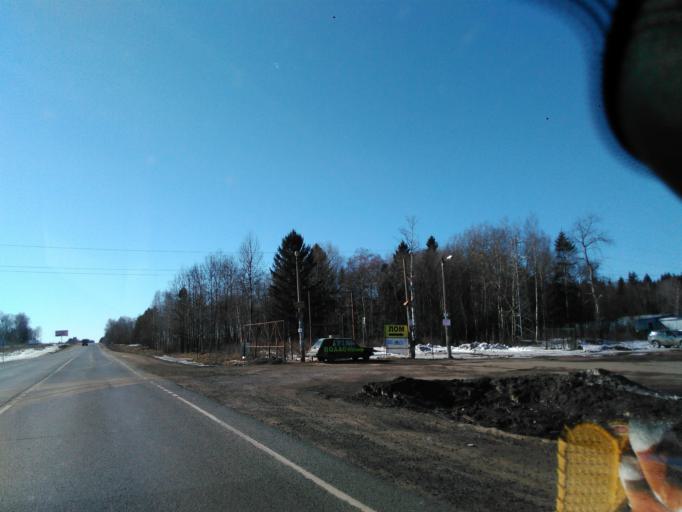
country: RU
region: Moskovskaya
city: Yermolino
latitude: 56.1353
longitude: 37.3975
